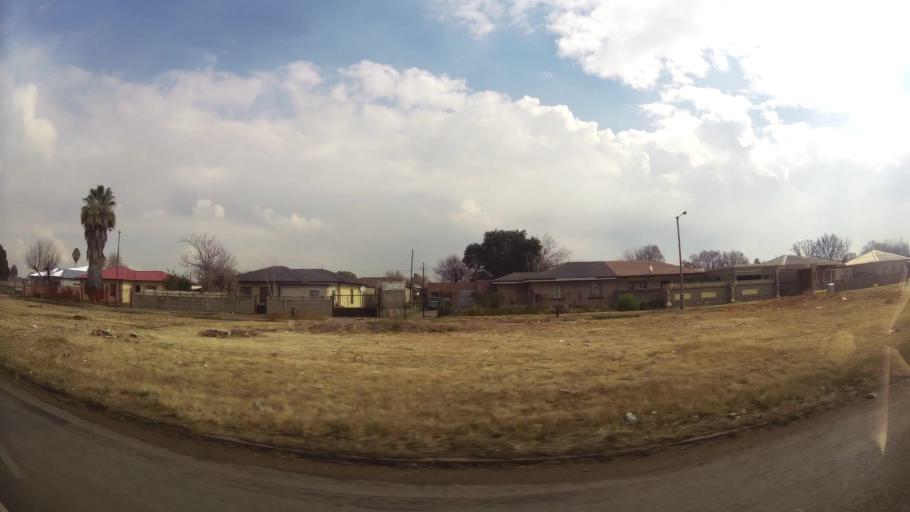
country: ZA
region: Gauteng
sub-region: Sedibeng District Municipality
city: Vereeniging
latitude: -26.6660
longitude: 27.9203
